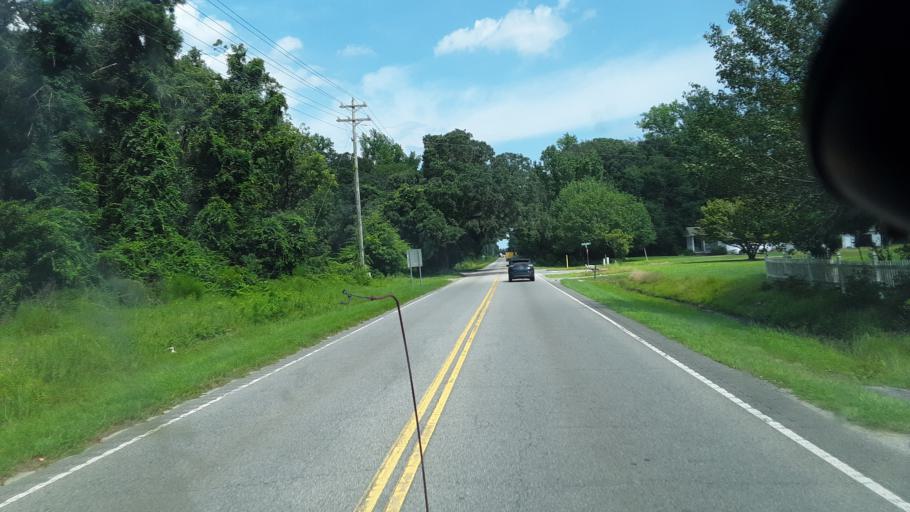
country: US
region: South Carolina
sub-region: Horry County
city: Red Hill
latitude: 33.8224
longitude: -78.9227
